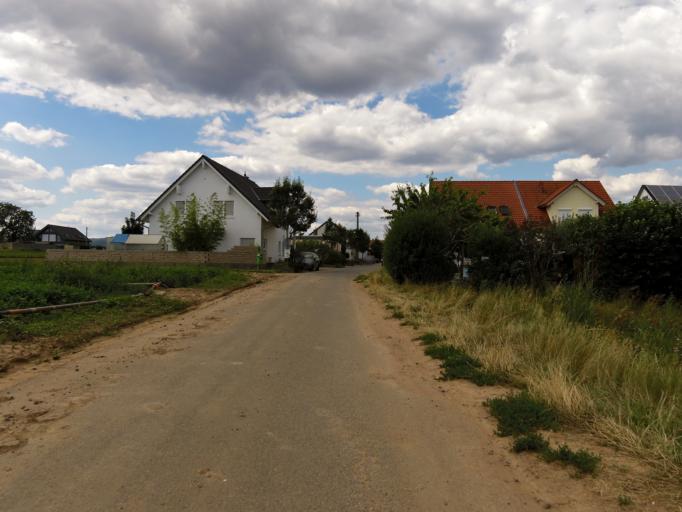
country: DE
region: Rheinland-Pfalz
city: Gonnheim
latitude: 49.4471
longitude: 8.2474
